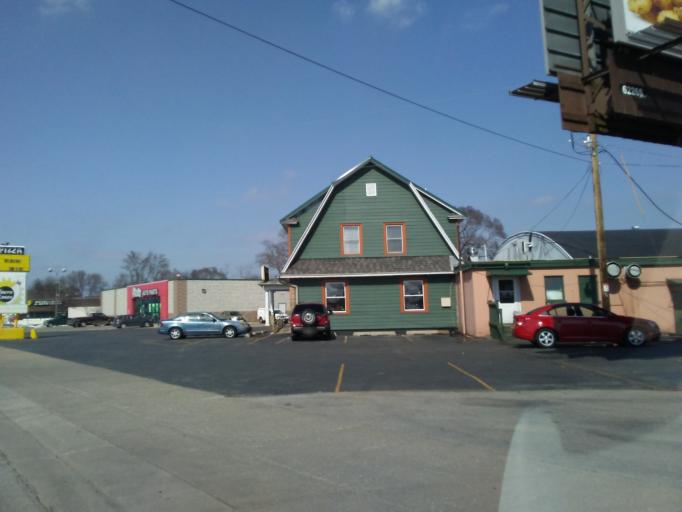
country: US
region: Wisconsin
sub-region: La Crosse County
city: La Crosse
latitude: 43.7734
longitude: -91.2180
